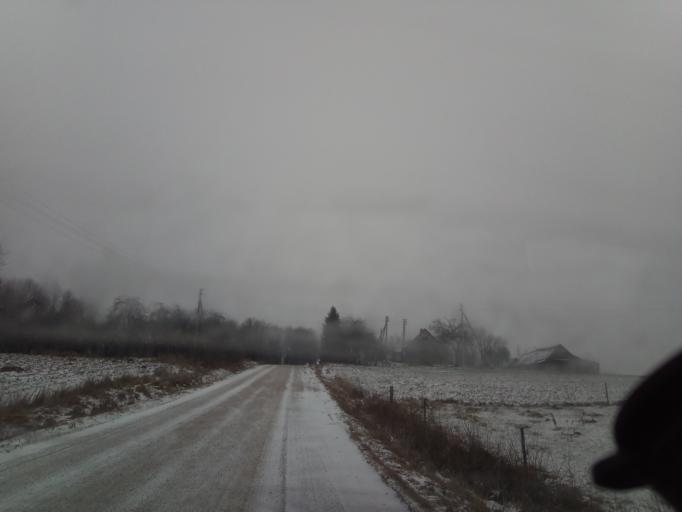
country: LT
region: Utenos apskritis
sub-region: Anyksciai
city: Anyksciai
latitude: 55.4425
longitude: 25.1038
